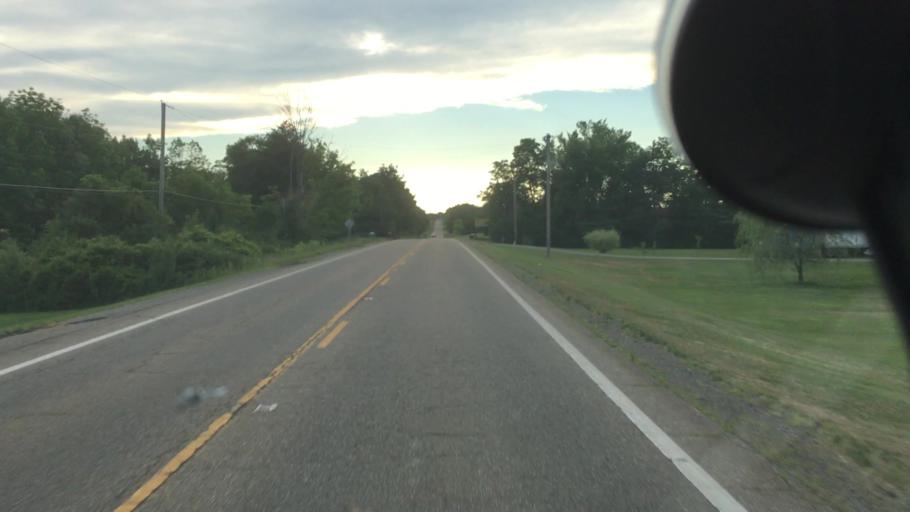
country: US
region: Ohio
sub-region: Columbiana County
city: East Palestine
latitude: 40.8538
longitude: -80.5284
